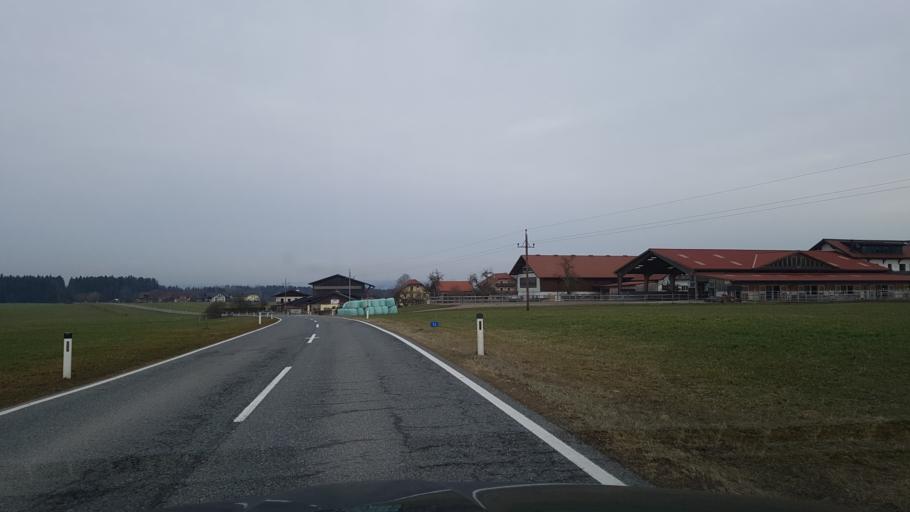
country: AT
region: Salzburg
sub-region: Politischer Bezirk Salzburg-Umgebung
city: Lamprechtshausen
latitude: 48.0236
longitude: 12.9590
